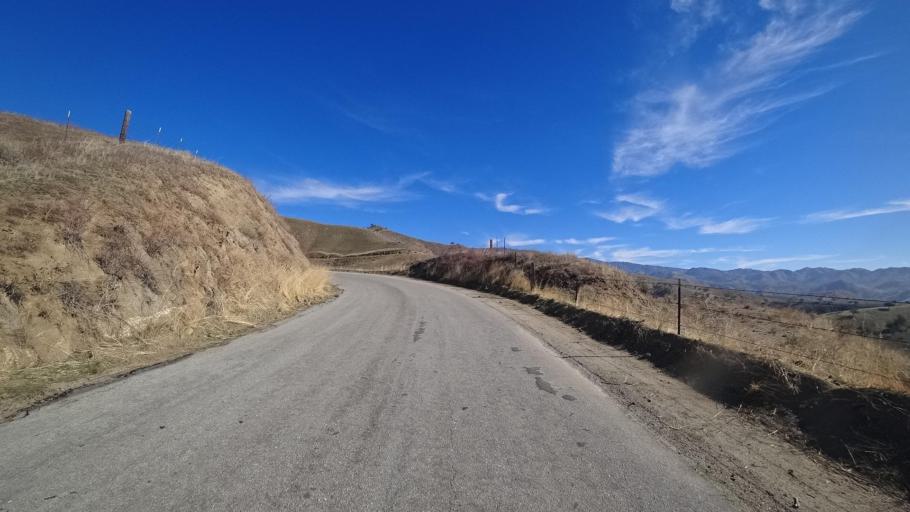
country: US
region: California
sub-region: Kern County
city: Arvin
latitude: 35.4231
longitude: -118.7341
